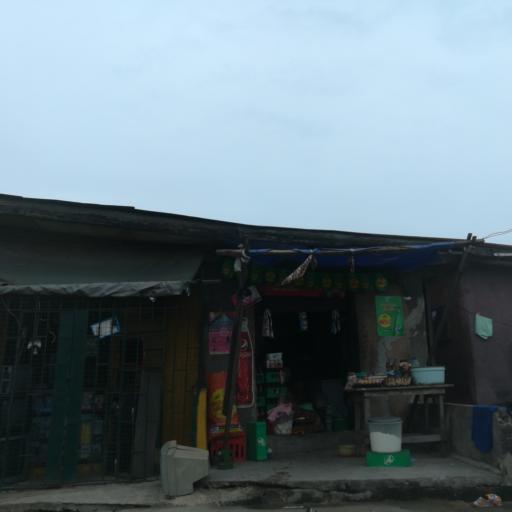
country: NG
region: Lagos
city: Makoko
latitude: 6.4976
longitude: 3.3866
